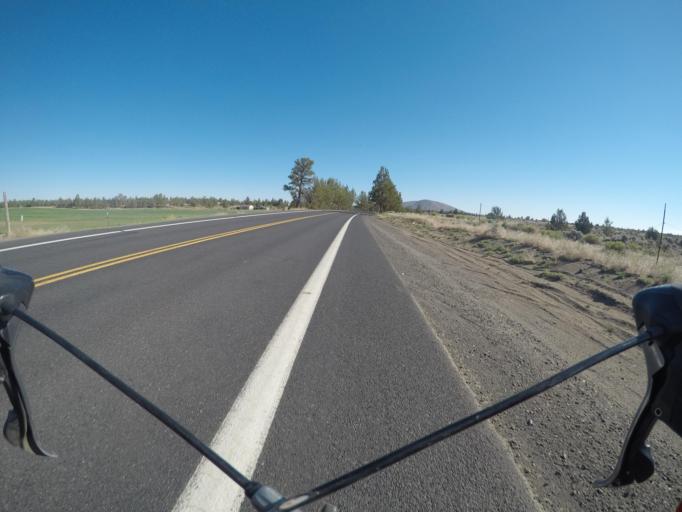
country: US
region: Oregon
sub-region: Deschutes County
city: Bend
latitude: 44.2082
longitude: -121.3188
